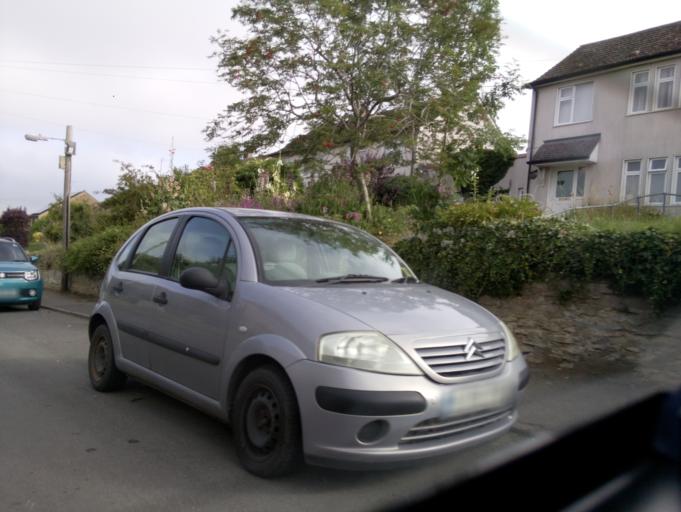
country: GB
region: England
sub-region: Borough of Swindon
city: Hannington
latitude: 51.6131
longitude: -1.7466
